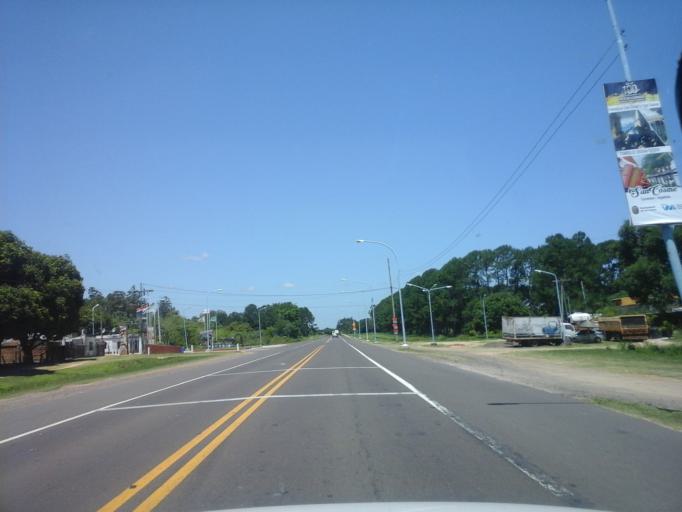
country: AR
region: Corrientes
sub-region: Departamento de San Cosme
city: San Cosme
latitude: -27.3737
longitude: -58.4885
